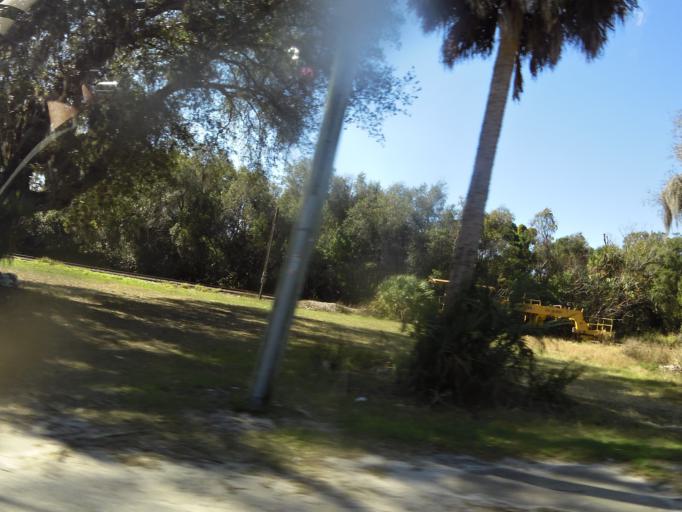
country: US
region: Florida
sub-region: Volusia County
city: Pierson
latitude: 29.3164
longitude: -81.4926
